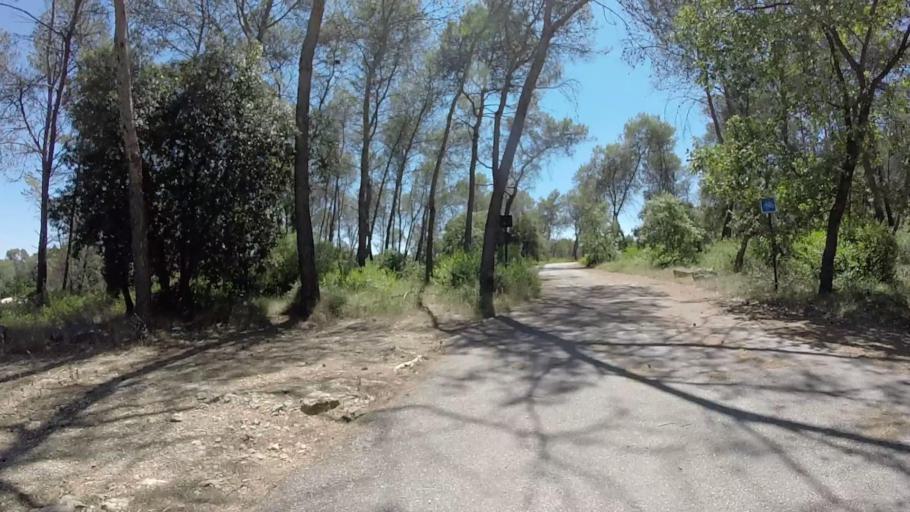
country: FR
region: Provence-Alpes-Cote d'Azur
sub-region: Departement des Alpes-Maritimes
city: Vallauris
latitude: 43.6087
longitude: 7.0523
